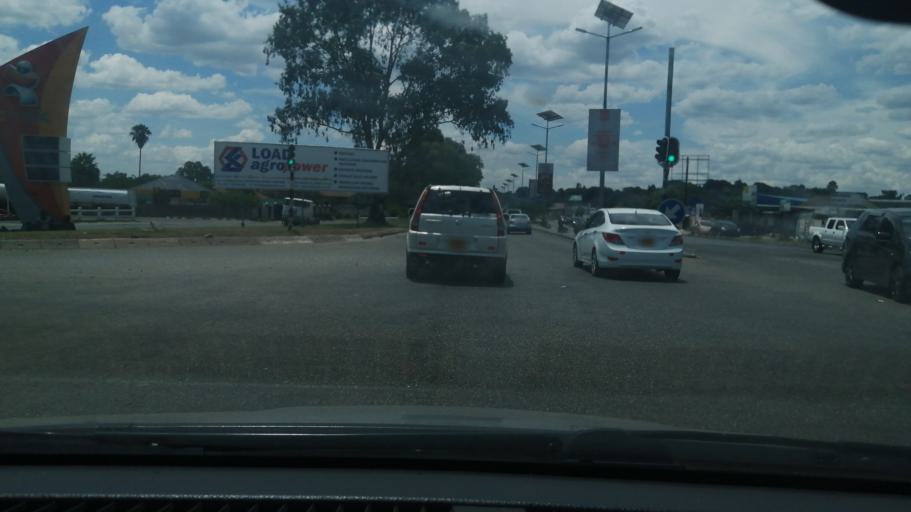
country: ZW
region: Harare
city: Harare
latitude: -17.8380
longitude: 31.1128
